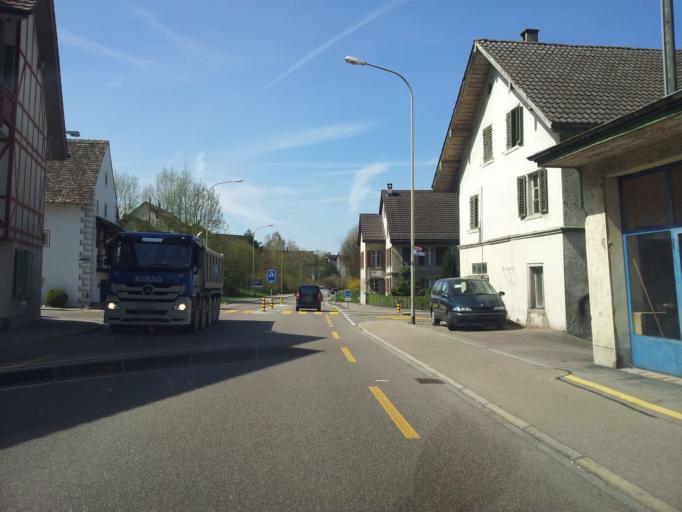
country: CH
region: Zurich
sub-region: Bezirk Dielsdorf
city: Regensdorf / Obstgarten
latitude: 47.4299
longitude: 8.4642
